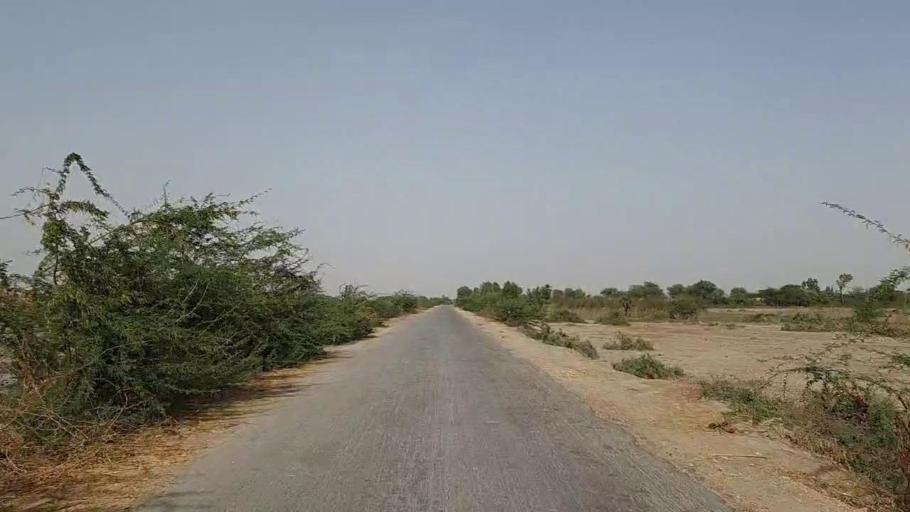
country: PK
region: Sindh
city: Tando Bago
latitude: 24.8974
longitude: 69.0793
